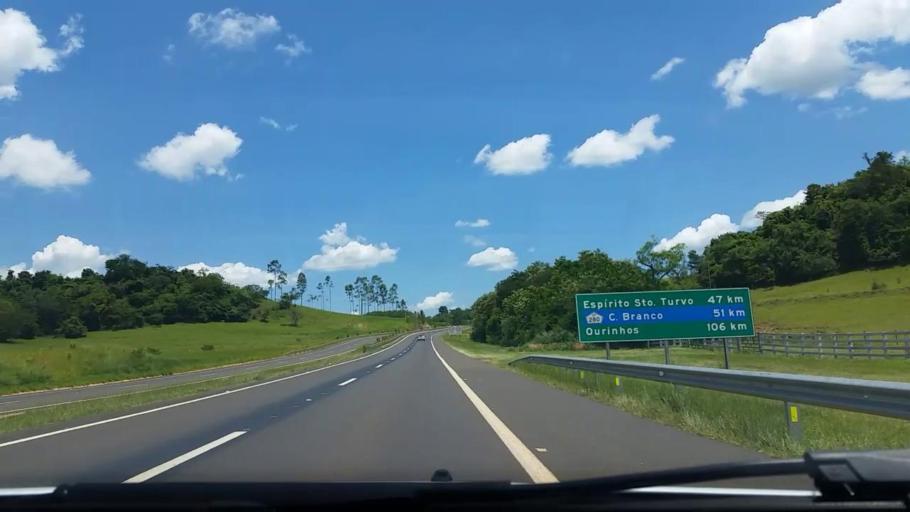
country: BR
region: Sao Paulo
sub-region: Bauru
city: Bauru
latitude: -22.4315
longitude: -49.1328
